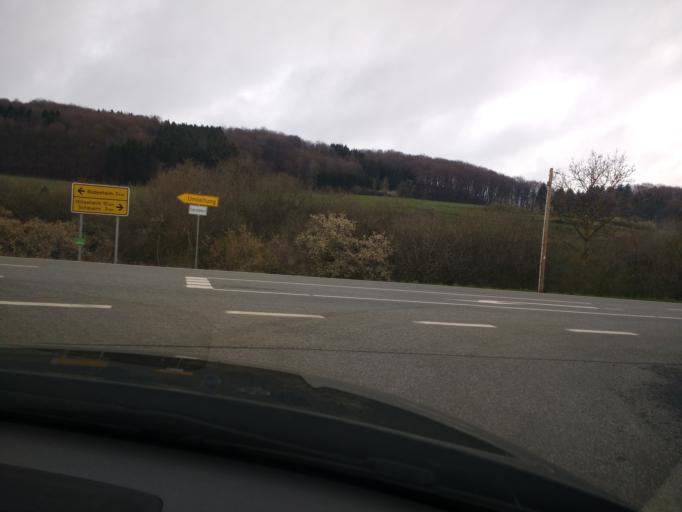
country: DE
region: Rheinland-Pfalz
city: Kalenborn-Scheuern
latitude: 50.2403
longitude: 6.5752
